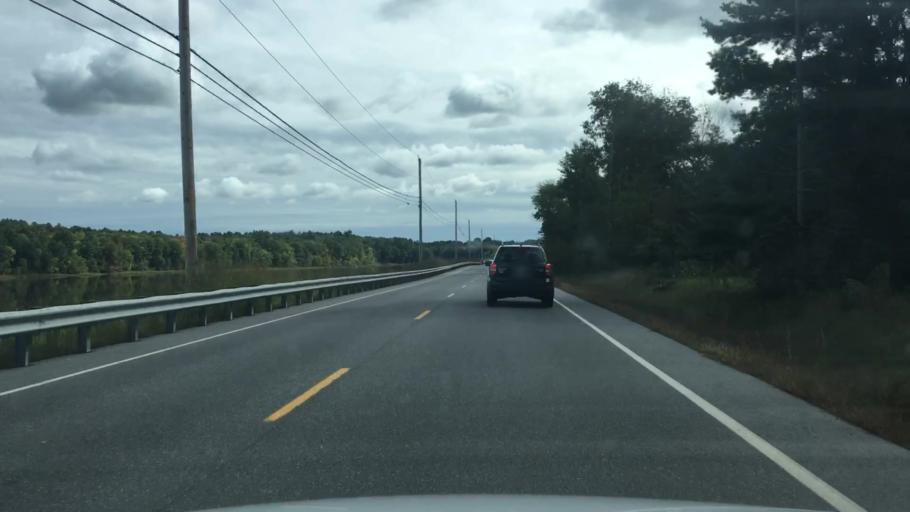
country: US
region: Maine
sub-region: Androscoggin County
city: Lisbon
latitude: 43.9946
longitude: -70.1431
